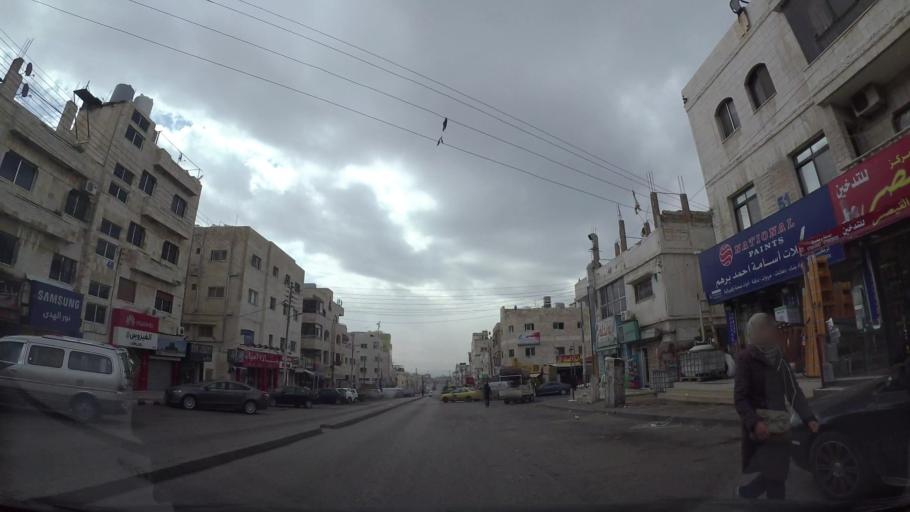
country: JO
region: Amman
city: Amman
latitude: 31.9834
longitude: 35.9241
